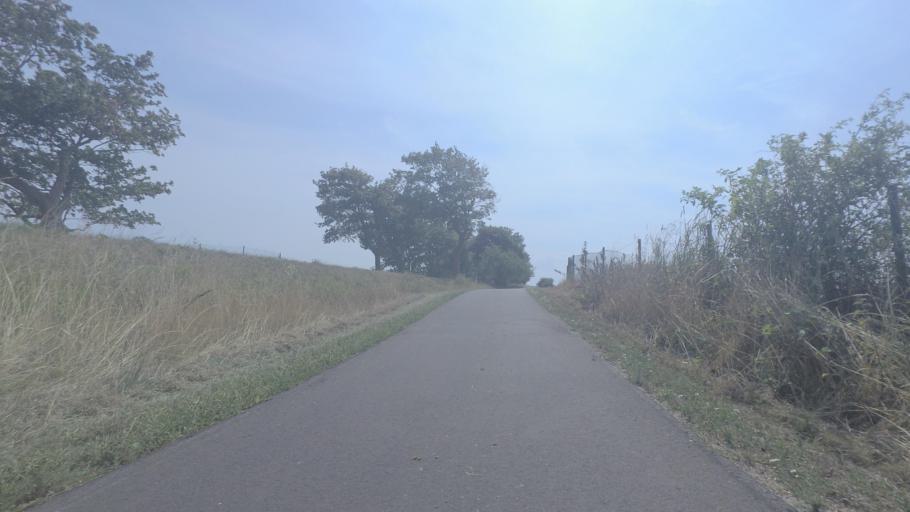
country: DE
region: Mecklenburg-Vorpommern
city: Garz
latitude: 54.2751
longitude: 13.3456
